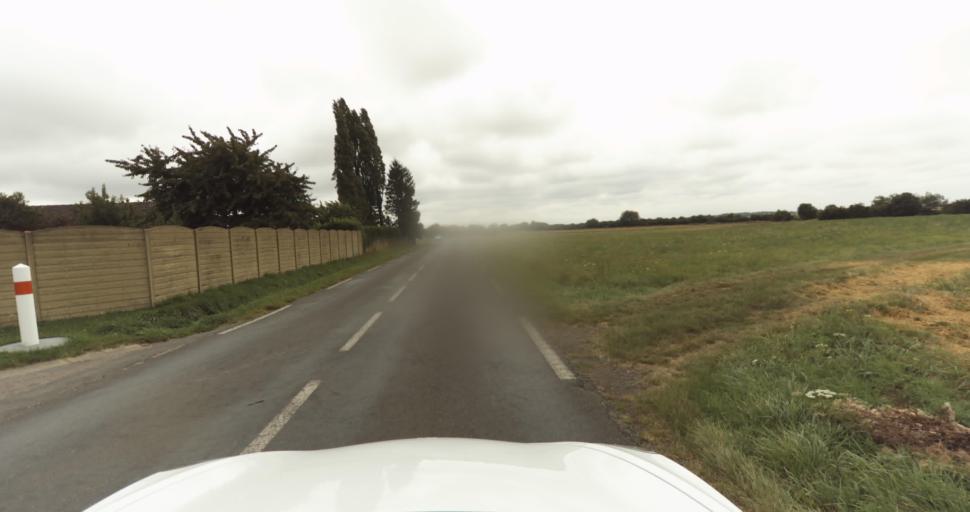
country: FR
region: Haute-Normandie
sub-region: Departement de l'Eure
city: Claville
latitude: 49.0703
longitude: 1.0674
